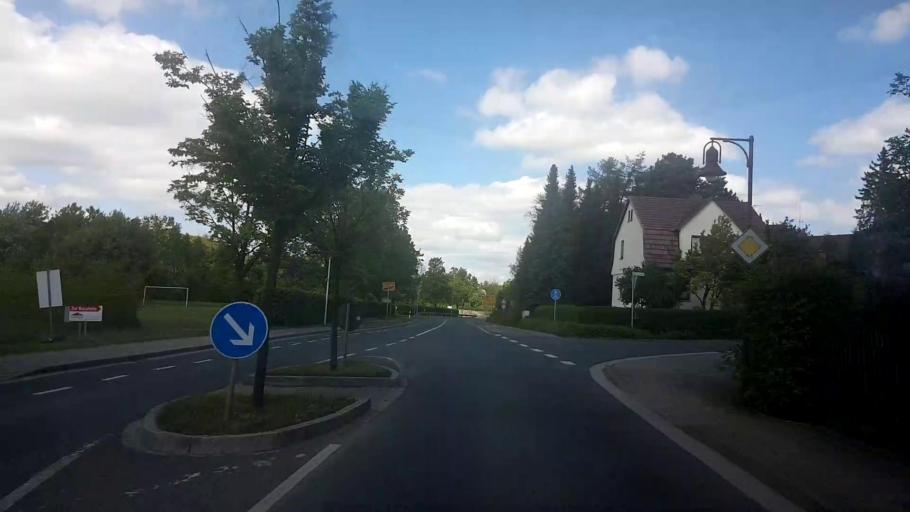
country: DE
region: Bavaria
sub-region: Upper Franconia
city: Niederfullbach
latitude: 50.2067
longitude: 10.9757
